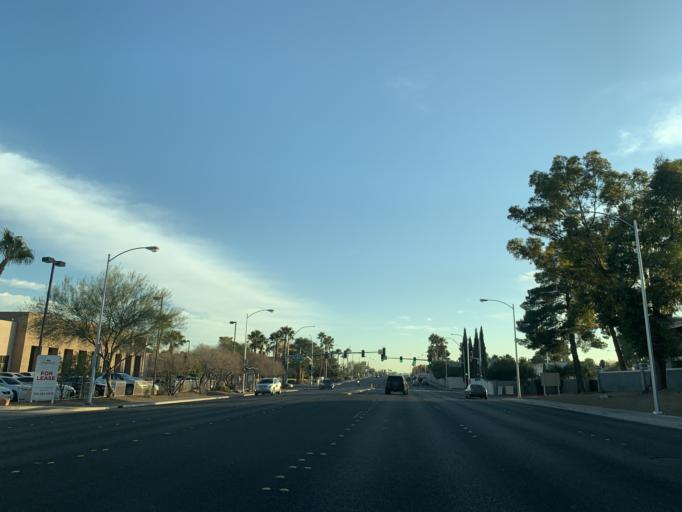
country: US
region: Nevada
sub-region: Clark County
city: Spring Valley
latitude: 36.0973
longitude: -115.2251
